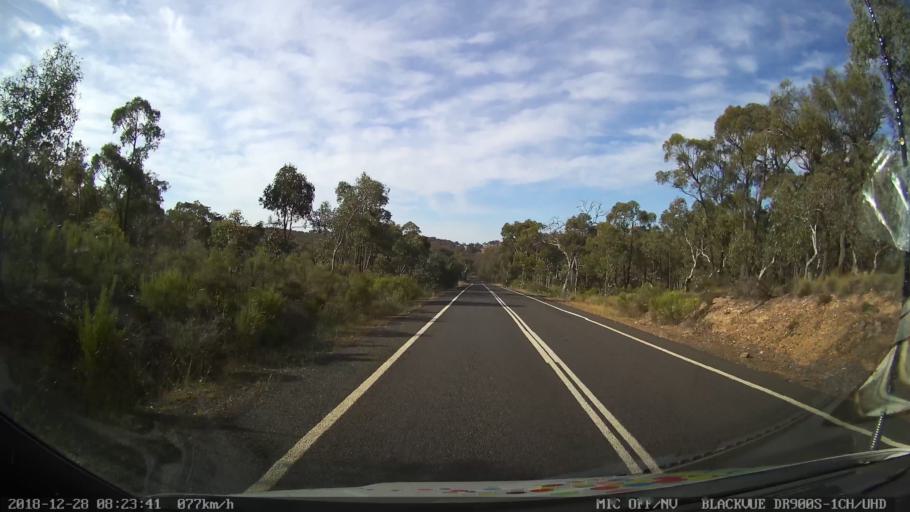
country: AU
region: New South Wales
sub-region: Blayney
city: Blayney
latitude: -33.9100
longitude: 149.3471
